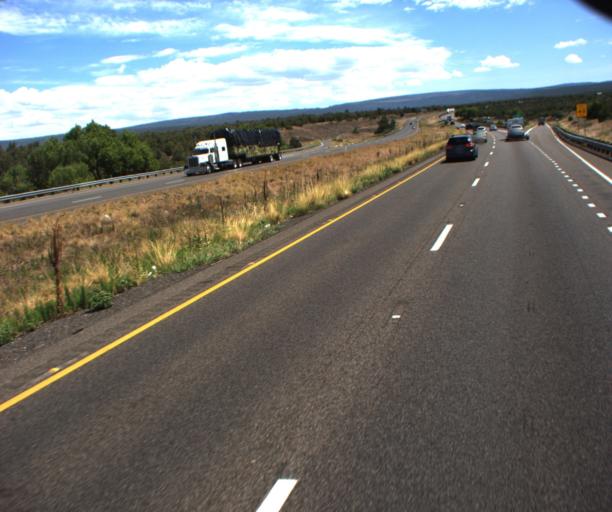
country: US
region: Arizona
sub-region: Yavapai County
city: Village of Oak Creek (Big Park)
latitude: 34.7616
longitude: -111.6595
